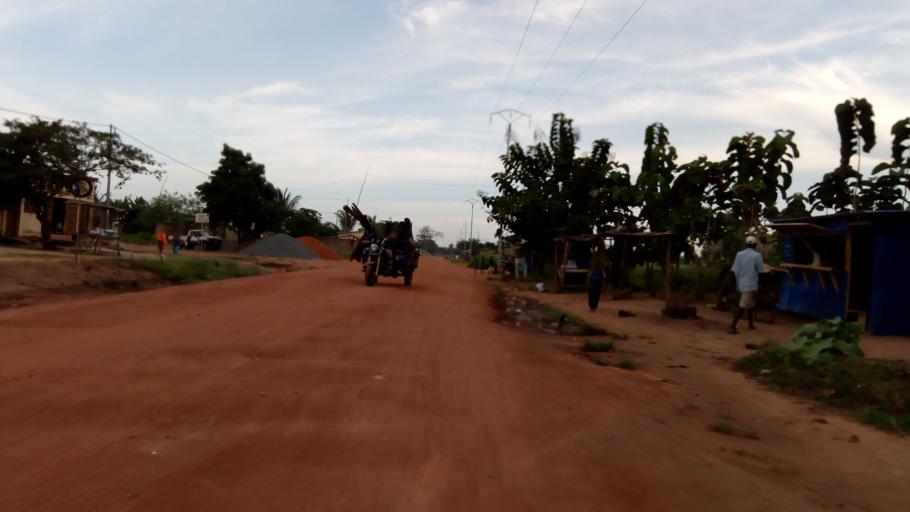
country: TG
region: Maritime
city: Lome
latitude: 6.2550
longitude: 1.1391
